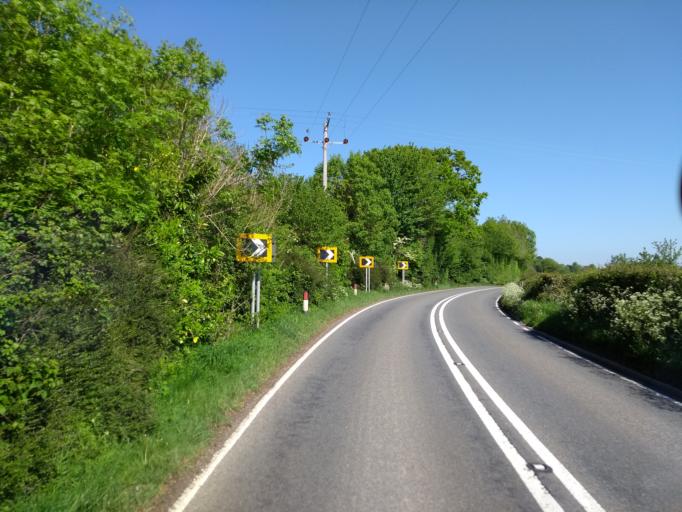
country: GB
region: England
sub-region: Somerset
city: Chard
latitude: 50.8429
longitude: -2.9596
